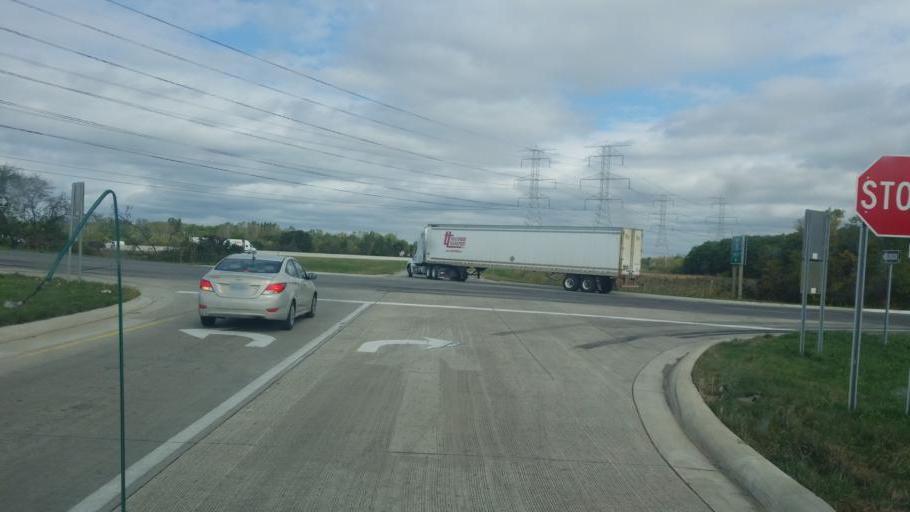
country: US
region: Michigan
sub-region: Monroe County
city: Detroit Beach
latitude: 41.9640
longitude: -83.3481
